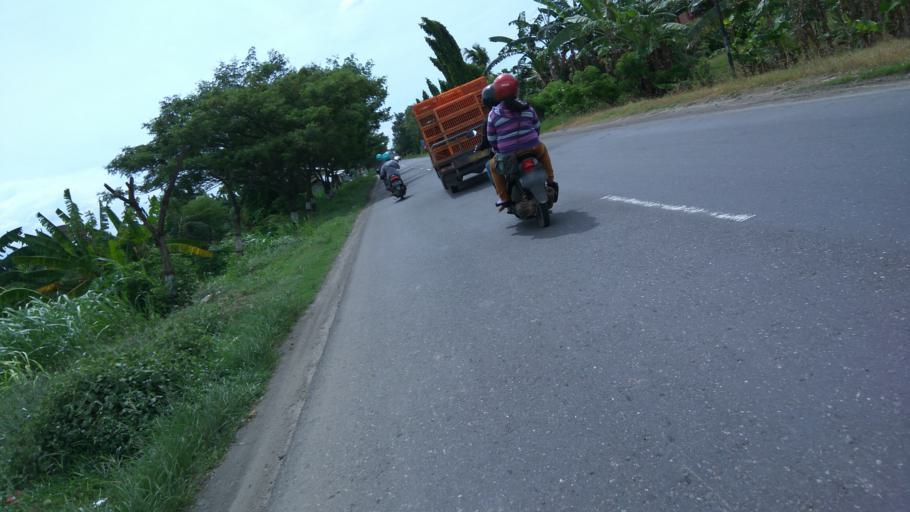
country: ID
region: Central Java
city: Mranggen
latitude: -7.0510
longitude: 110.6486
